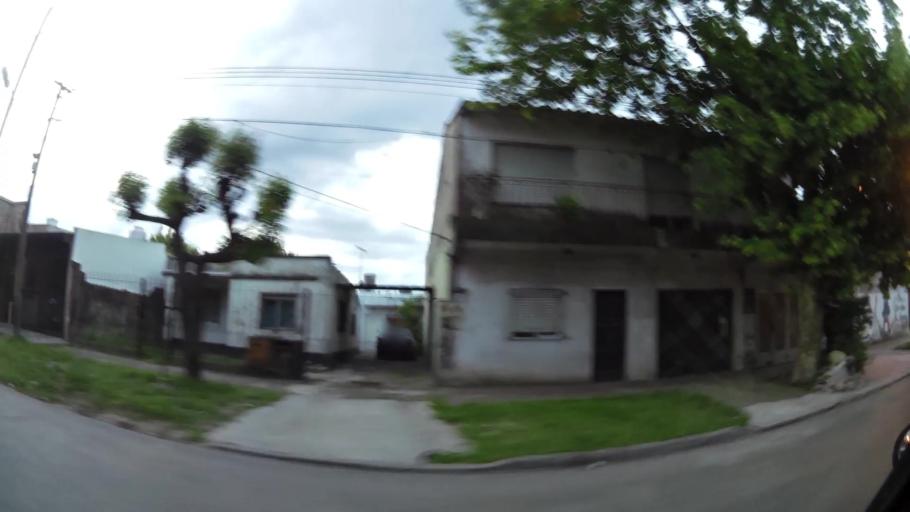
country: AR
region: Buenos Aires
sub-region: Partido de Quilmes
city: Quilmes
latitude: -34.7361
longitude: -58.2318
